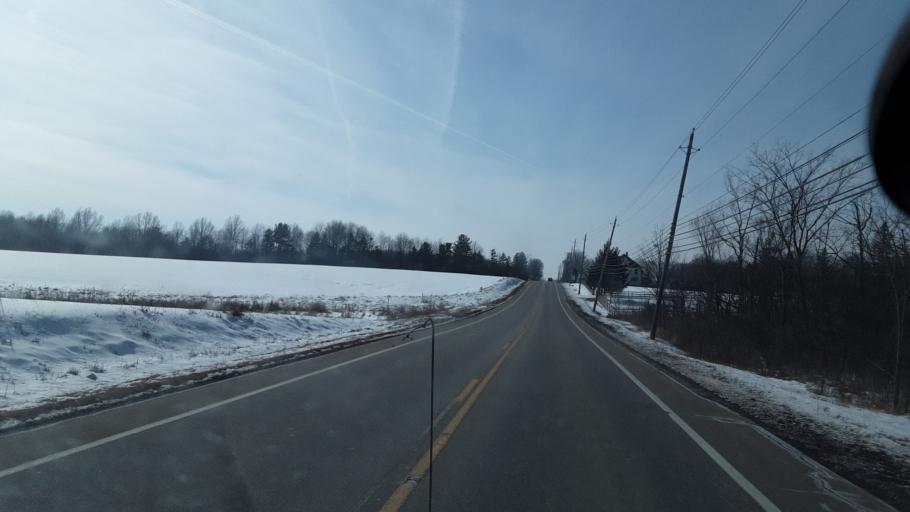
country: US
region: Ohio
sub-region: Mahoning County
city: Canfield
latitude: 41.0245
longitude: -80.8206
